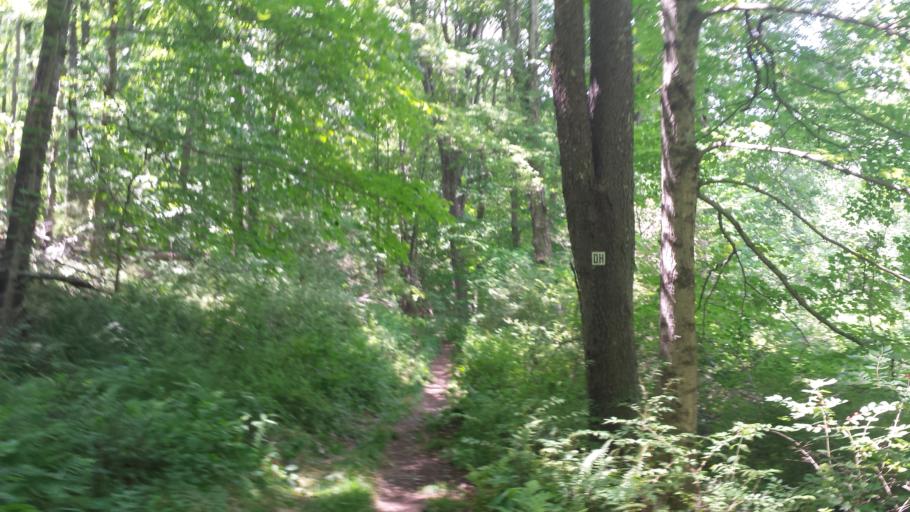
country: US
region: New York
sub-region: Westchester County
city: Pound Ridge
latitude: 41.2719
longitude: -73.5798
